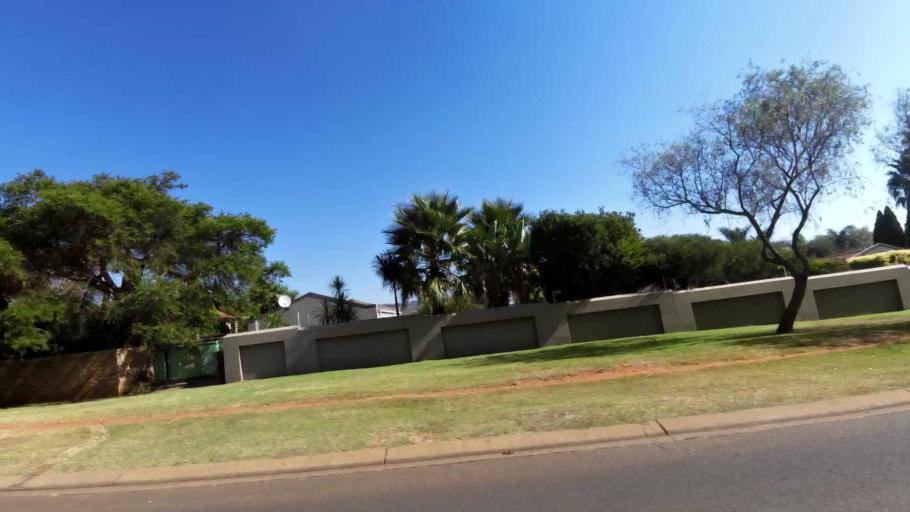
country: ZA
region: Gauteng
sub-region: City of Johannesburg Metropolitan Municipality
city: Roodepoort
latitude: -26.1436
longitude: 27.9362
